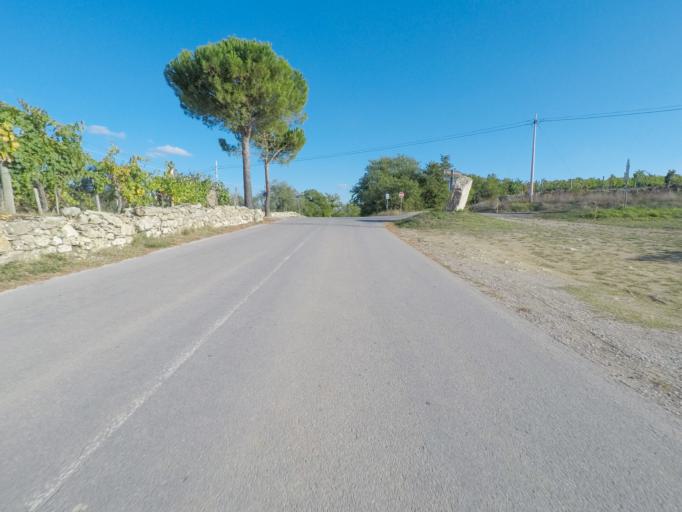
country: IT
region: Tuscany
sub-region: Provincia di Siena
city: Radda in Chianti
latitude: 43.4516
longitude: 11.3904
